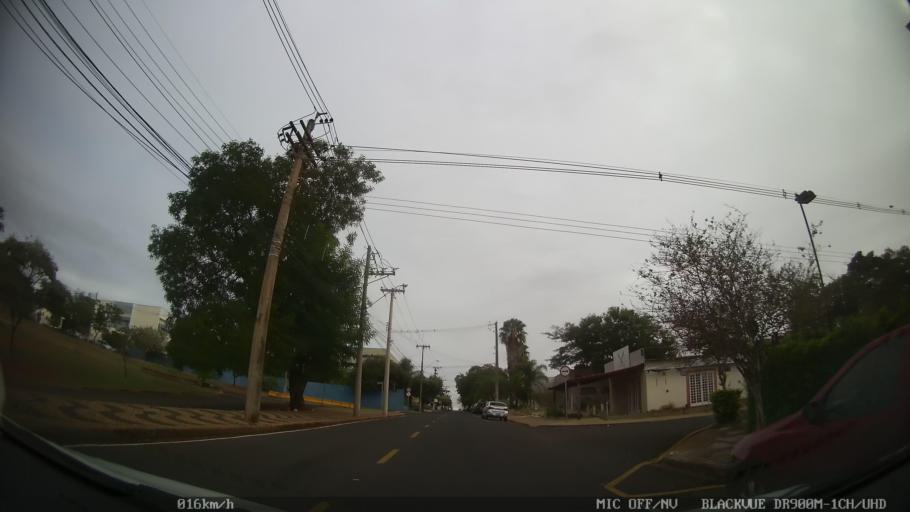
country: BR
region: Sao Paulo
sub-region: Sao Jose Do Rio Preto
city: Sao Jose do Rio Preto
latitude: -20.8307
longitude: -49.3932
